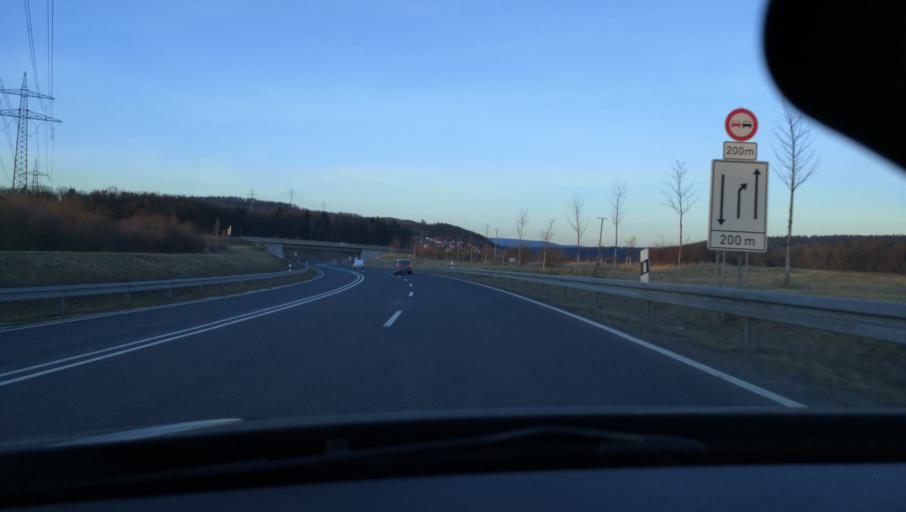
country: DE
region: Bavaria
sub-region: Upper Franconia
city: Rodental
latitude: 50.2998
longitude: 11.0105
